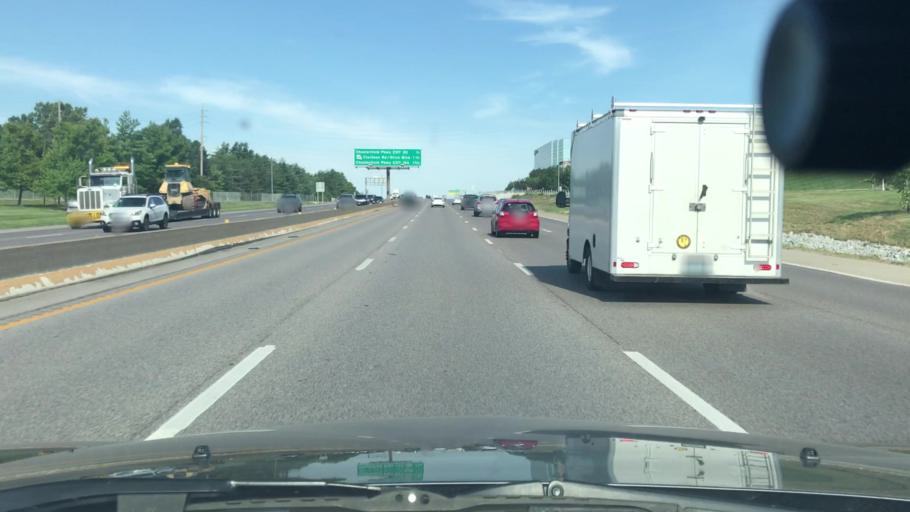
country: US
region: Missouri
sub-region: Saint Louis County
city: Chesterfield
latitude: 38.6469
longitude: -90.5311
